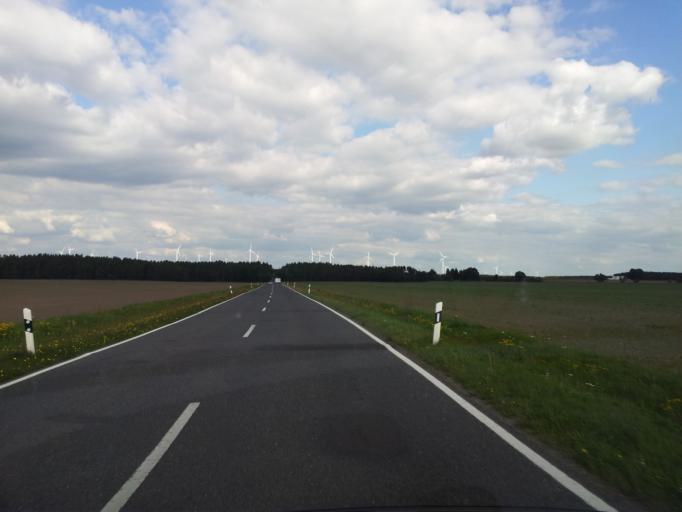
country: DE
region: Brandenburg
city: Sallgast
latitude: 51.6053
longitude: 13.7944
